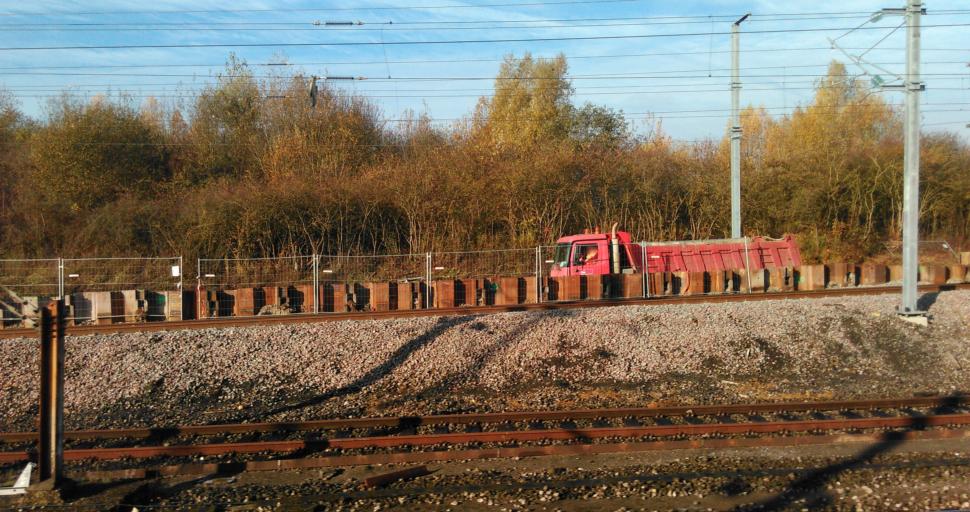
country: LU
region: Luxembourg
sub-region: Canton de Luxembourg
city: Hesperange
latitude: 49.5848
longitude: 6.1351
